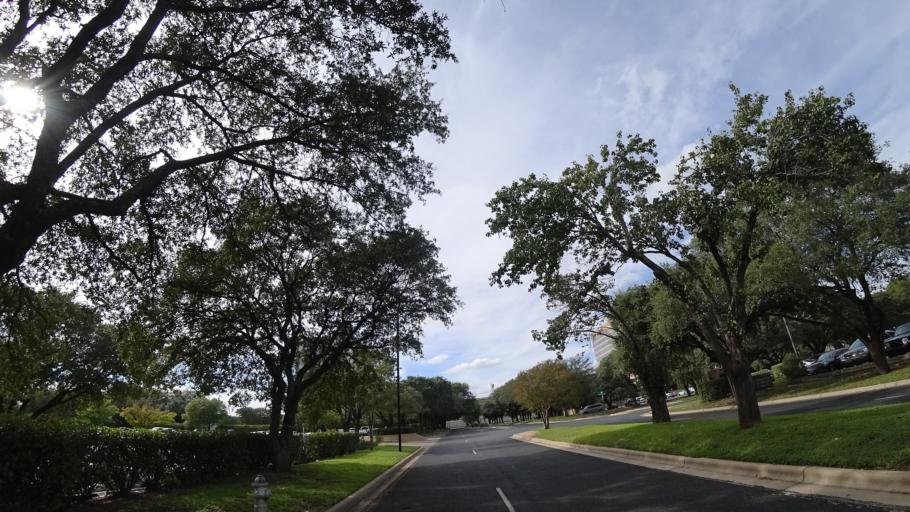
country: US
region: Texas
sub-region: Travis County
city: Austin
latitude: 30.2130
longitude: -97.7500
